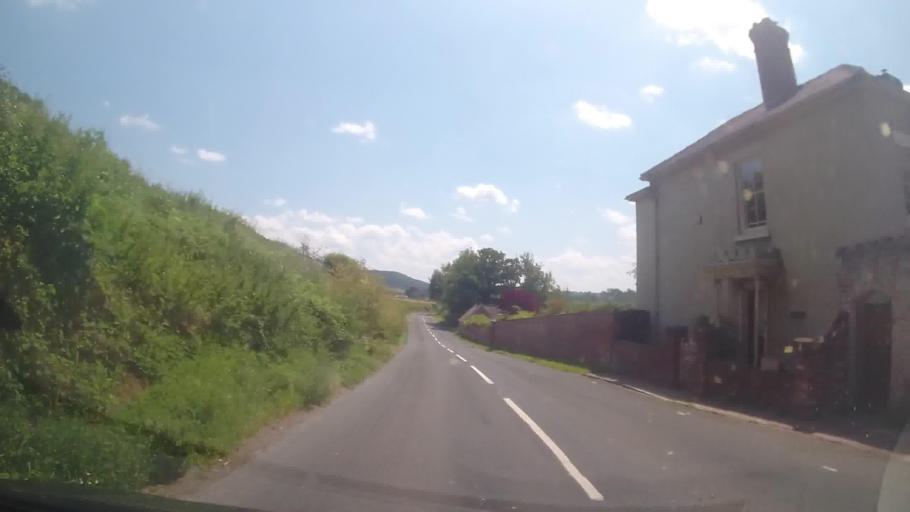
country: GB
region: England
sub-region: Herefordshire
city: Brockhampton
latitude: 52.0162
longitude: -2.6254
